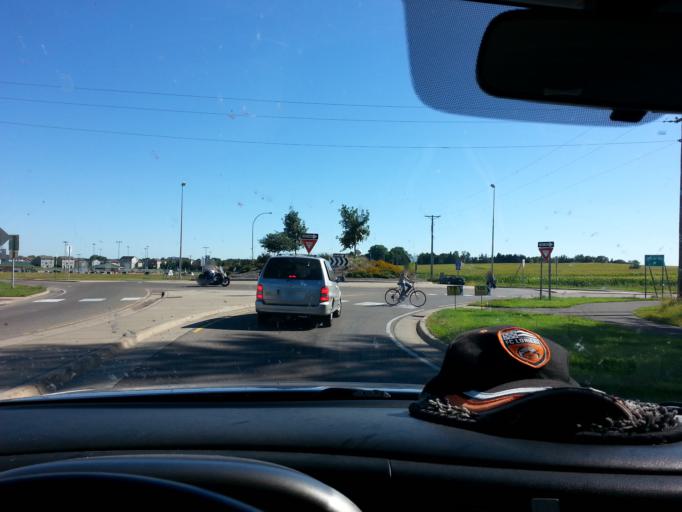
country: US
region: Minnesota
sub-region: Dakota County
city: Farmington
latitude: 44.6743
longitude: -93.1367
